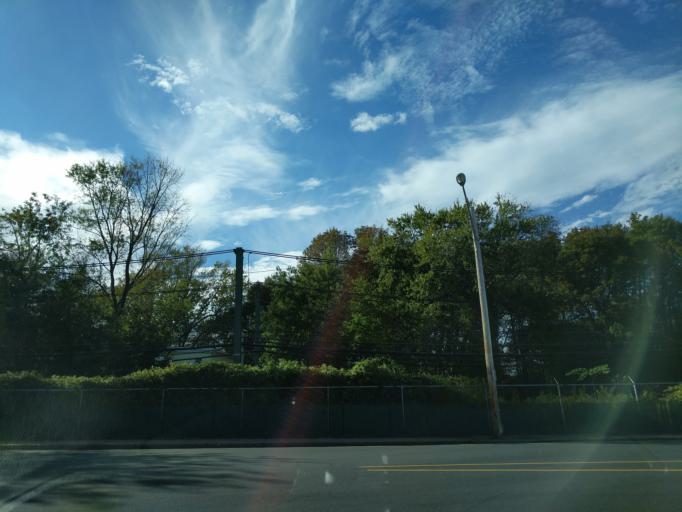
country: US
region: Massachusetts
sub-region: Suffolk County
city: Revere
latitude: 42.3989
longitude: -70.9911
